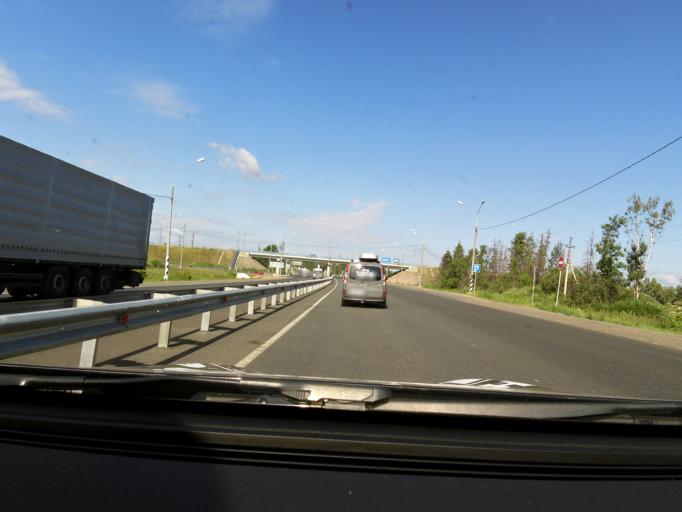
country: RU
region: Tverskaya
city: Emmaus
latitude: 56.7837
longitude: 36.0923
